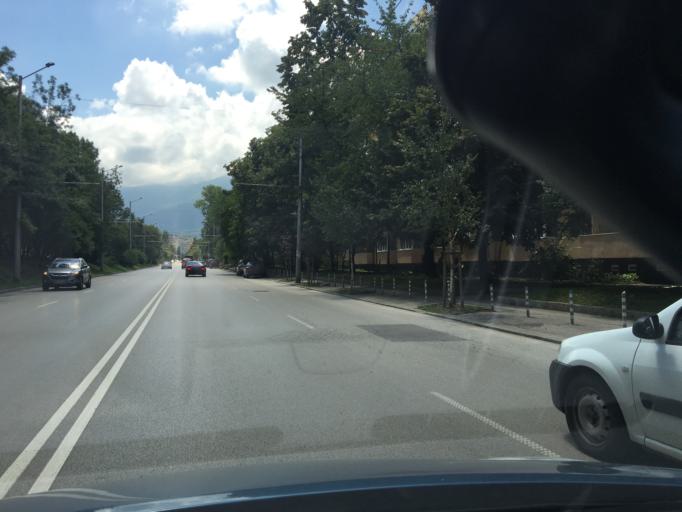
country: BG
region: Sofia-Capital
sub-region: Stolichna Obshtina
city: Sofia
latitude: 42.6720
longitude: 23.3043
